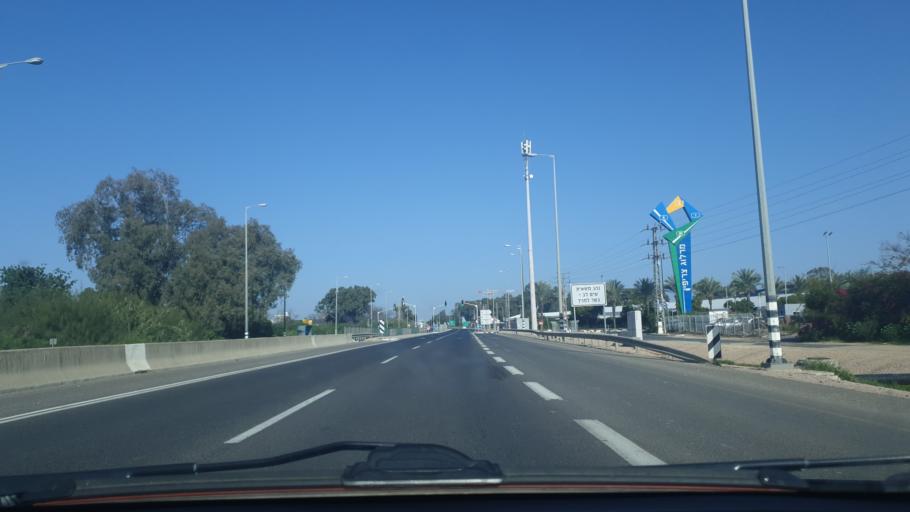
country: IL
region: Central District
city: Kefar Habad
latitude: 31.9625
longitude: 34.8496
